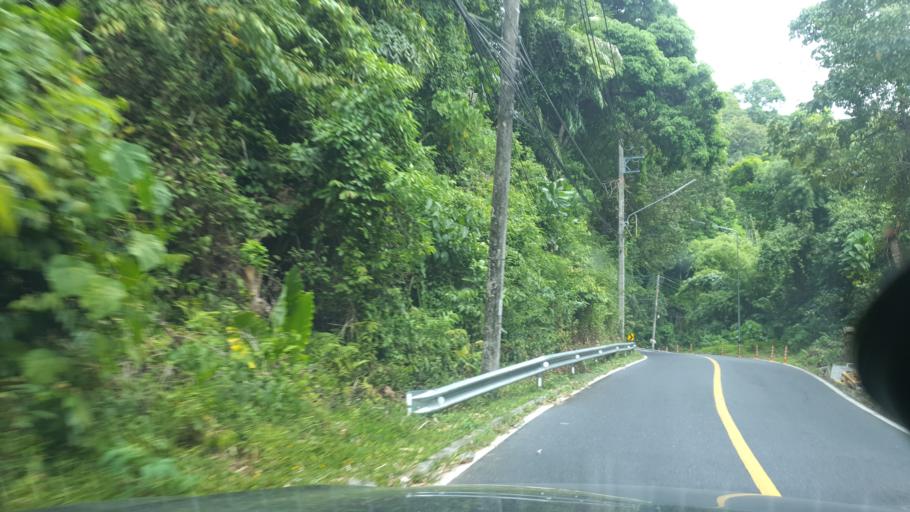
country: TH
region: Phuket
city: Thalang
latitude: 8.0438
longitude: 98.2780
